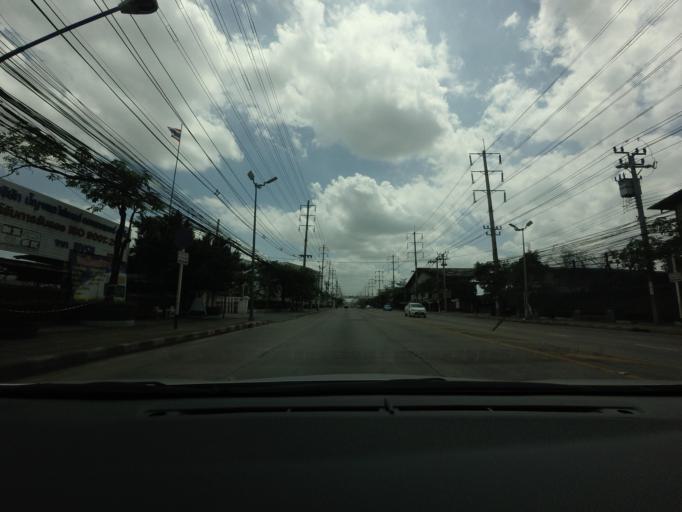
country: TH
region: Samut Prakan
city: Phra Pradaeng
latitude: 13.6470
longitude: 100.5740
